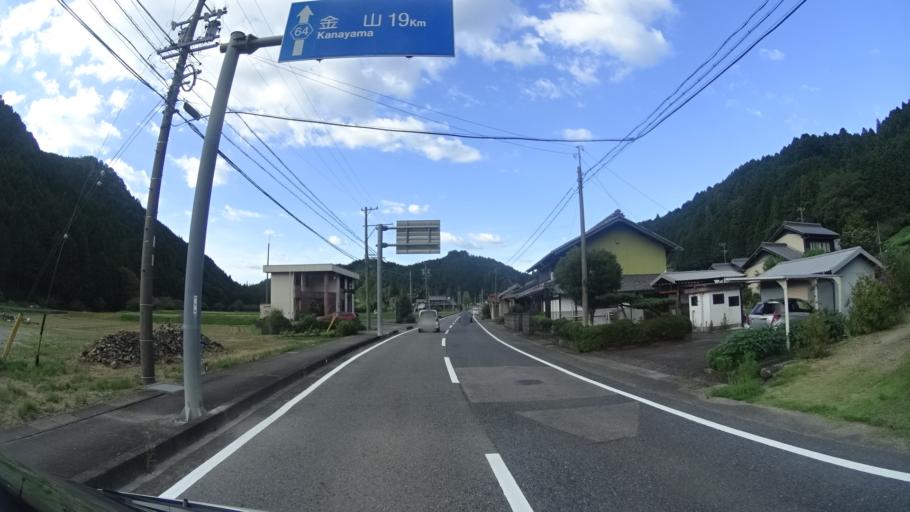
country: JP
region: Gifu
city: Minokamo
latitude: 35.5684
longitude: 137.0836
